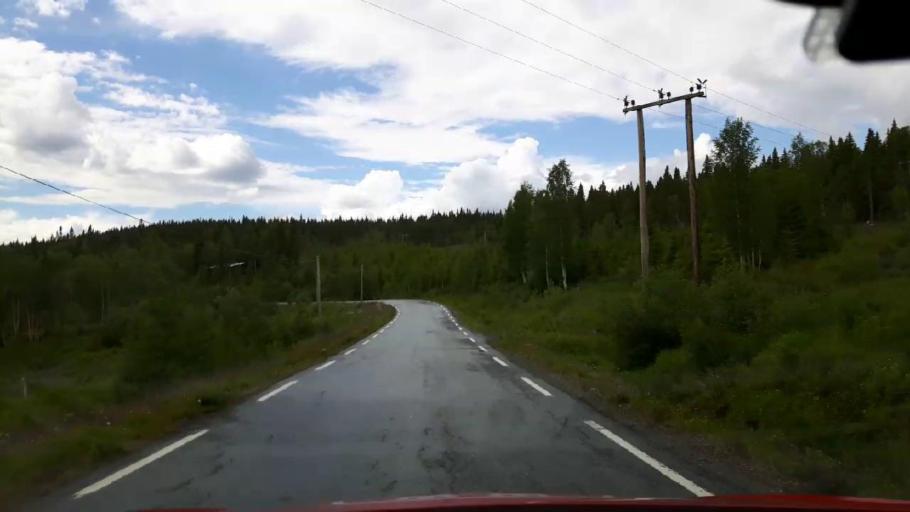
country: NO
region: Nord-Trondelag
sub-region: Lierne
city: Sandvika
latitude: 64.1027
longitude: 14.0218
